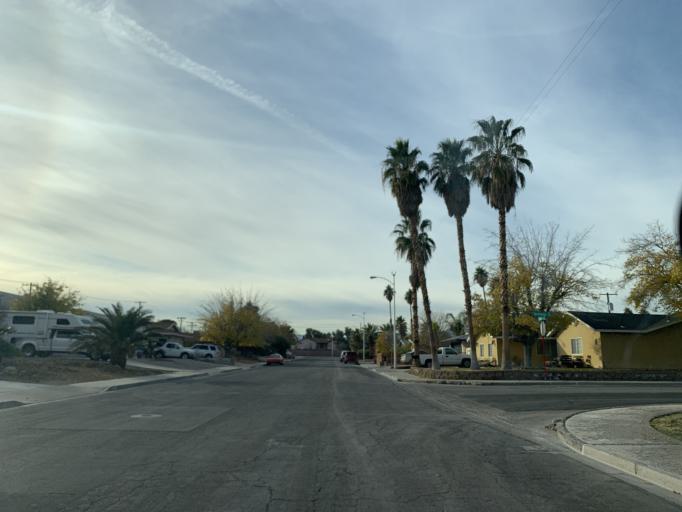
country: US
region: Nevada
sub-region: Clark County
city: Las Vegas
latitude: 36.1475
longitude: -115.1712
